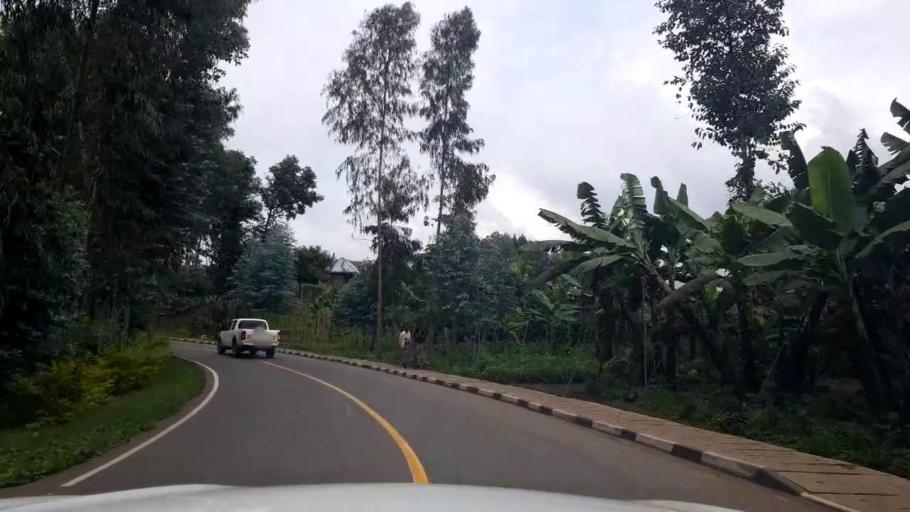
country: RW
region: Northern Province
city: Musanze
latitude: -1.4533
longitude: 29.6081
